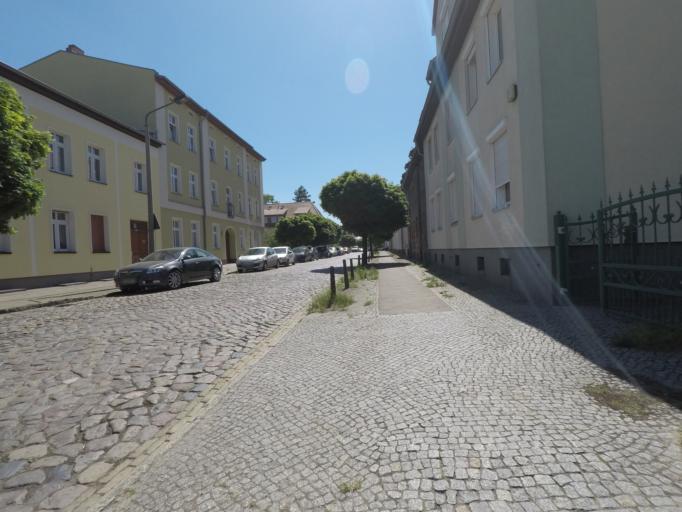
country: DE
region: Brandenburg
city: Melchow
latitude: 52.8366
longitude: 13.7328
